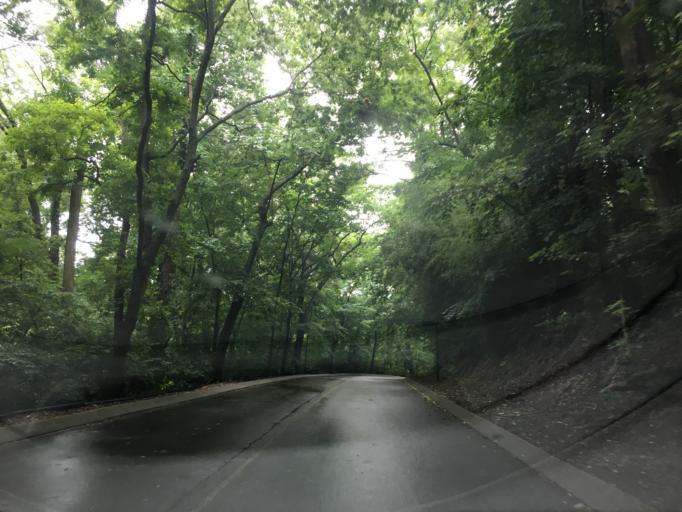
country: US
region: Tennessee
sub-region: Davidson County
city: Belle Meade
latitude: 36.0732
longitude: -86.8971
